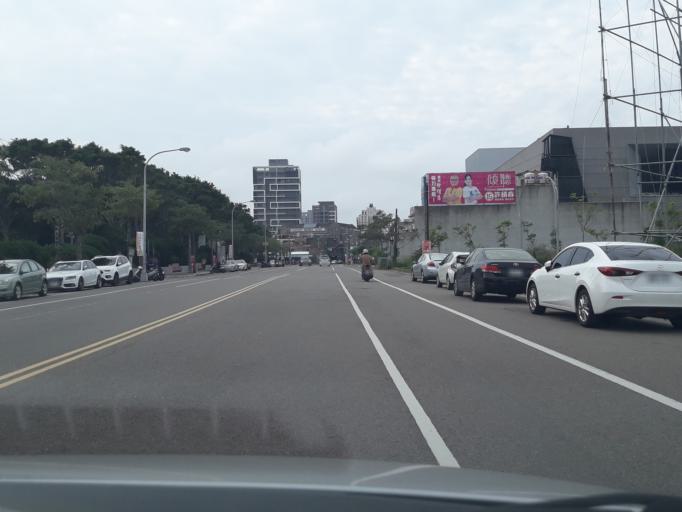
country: TW
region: Taiwan
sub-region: Hsinchu
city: Hsinchu
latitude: 24.6907
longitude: 120.8881
